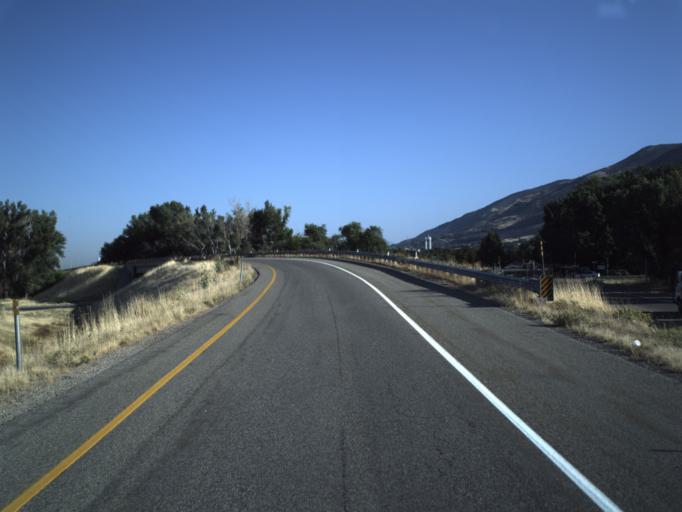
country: US
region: Utah
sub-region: Davis County
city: Farmington
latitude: 40.9718
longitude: -111.8920
